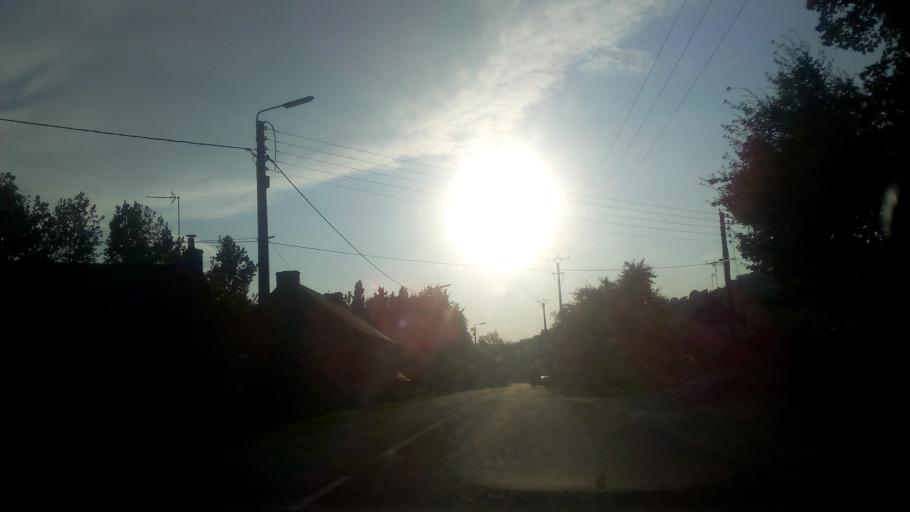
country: FR
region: Brittany
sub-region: Departement du Morbihan
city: Saint-Jean-la-Poterie
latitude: 47.6260
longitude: -2.1026
